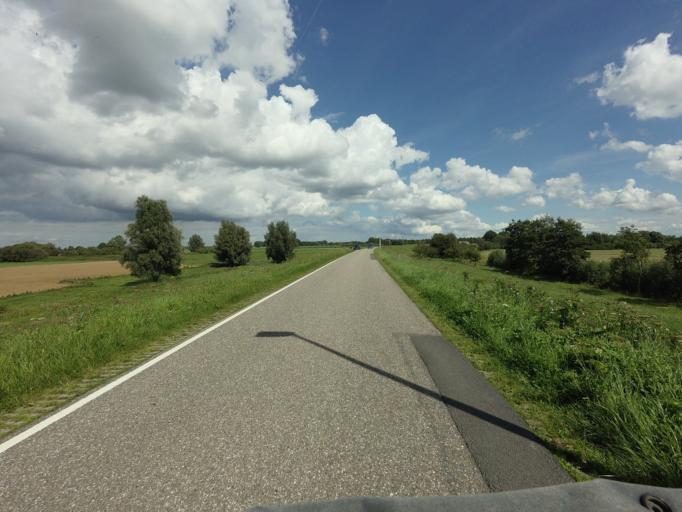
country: NL
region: Utrecht
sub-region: Gemeente Vianen
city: Vianen
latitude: 51.9772
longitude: 5.0567
